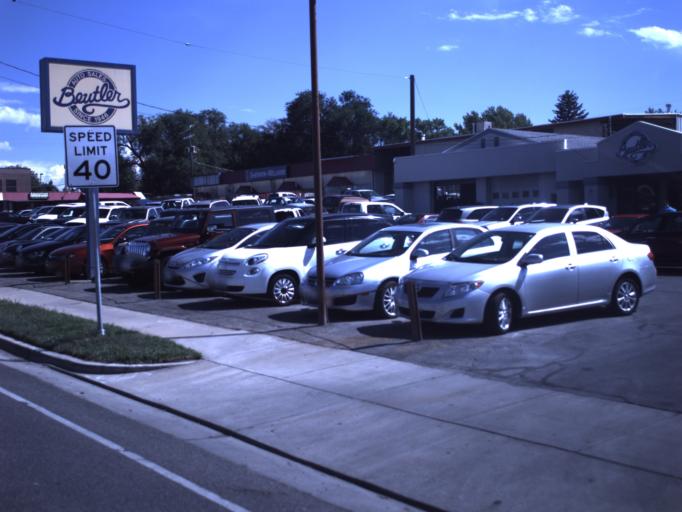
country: US
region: Utah
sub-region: Davis County
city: Clearfield
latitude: 41.1190
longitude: -112.0260
